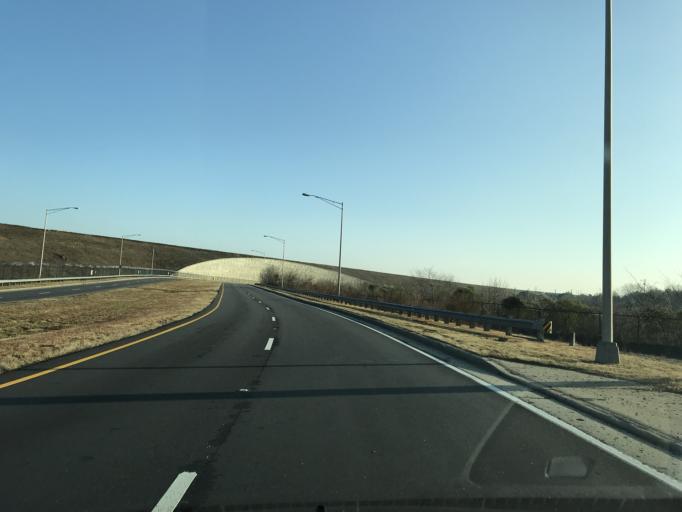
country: US
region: Georgia
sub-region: Fulton County
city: College Park
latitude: 33.6174
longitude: -84.4434
